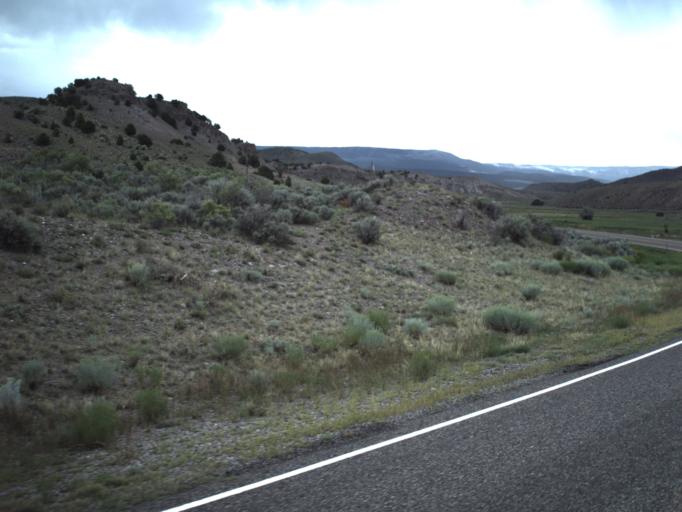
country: US
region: Utah
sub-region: Piute County
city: Junction
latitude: 38.1789
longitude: -112.0784
